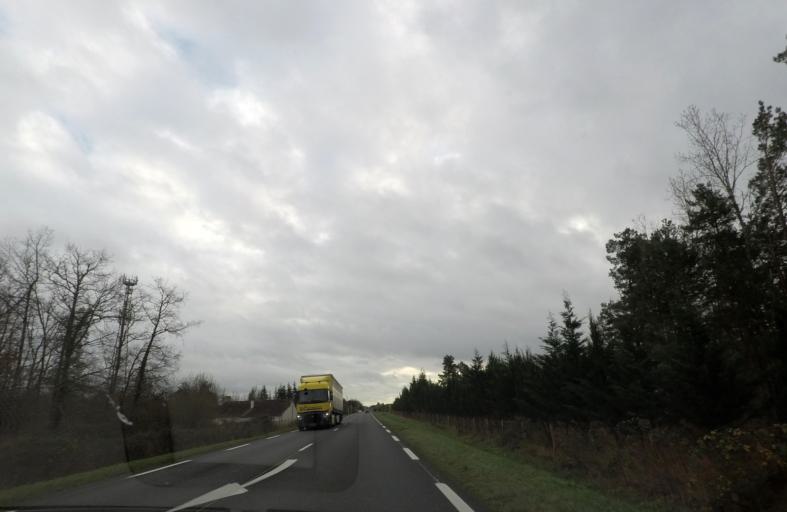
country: FR
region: Centre
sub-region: Departement du Loir-et-Cher
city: Soings-en-Sologne
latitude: 47.4670
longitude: 1.5120
